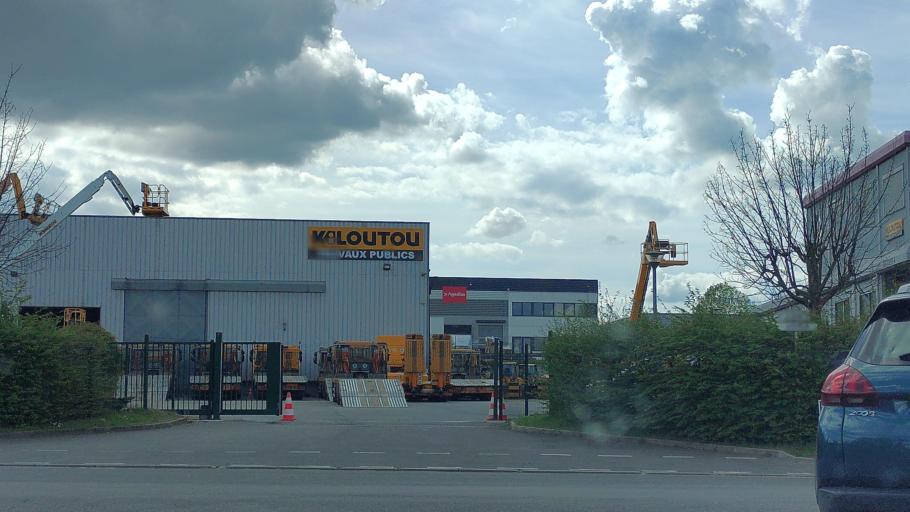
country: FR
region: Ile-de-France
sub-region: Departement du Val-d'Oise
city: Saint-Ouen-l'Aumone
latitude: 49.0518
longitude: 2.1469
